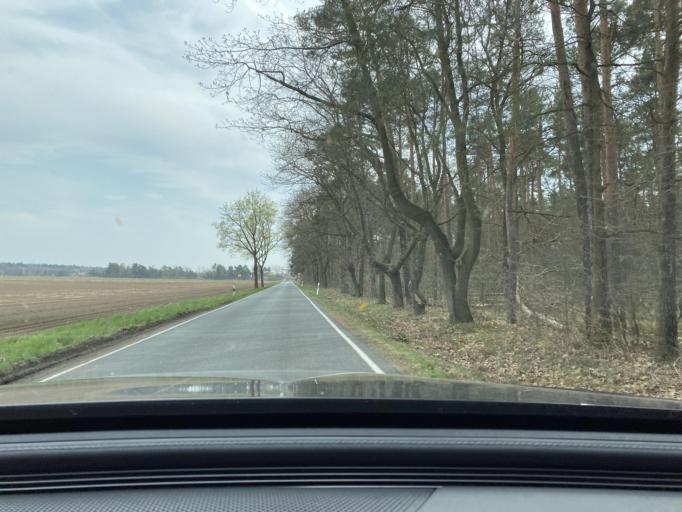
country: DE
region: Saxony
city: Konigswartha
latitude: 51.3057
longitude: 14.3140
